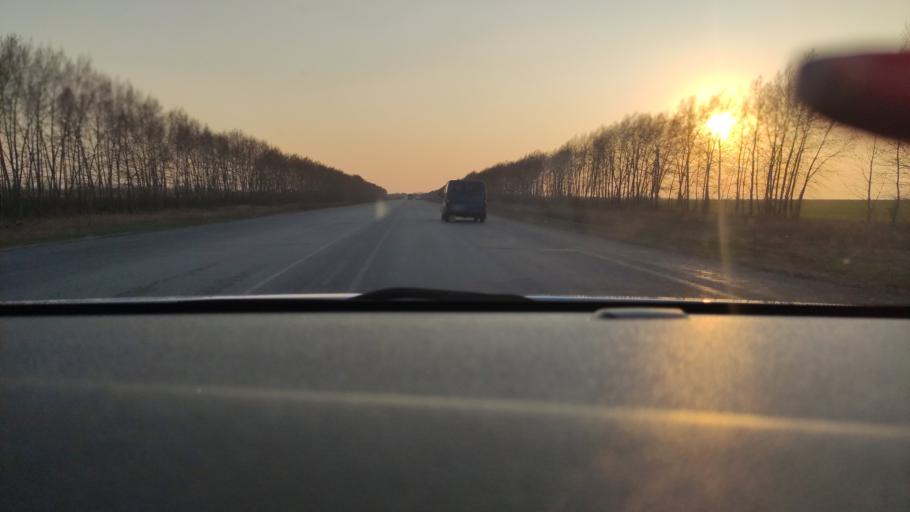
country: RU
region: Voronezj
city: Kolodeznyy
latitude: 51.4161
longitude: 39.2717
